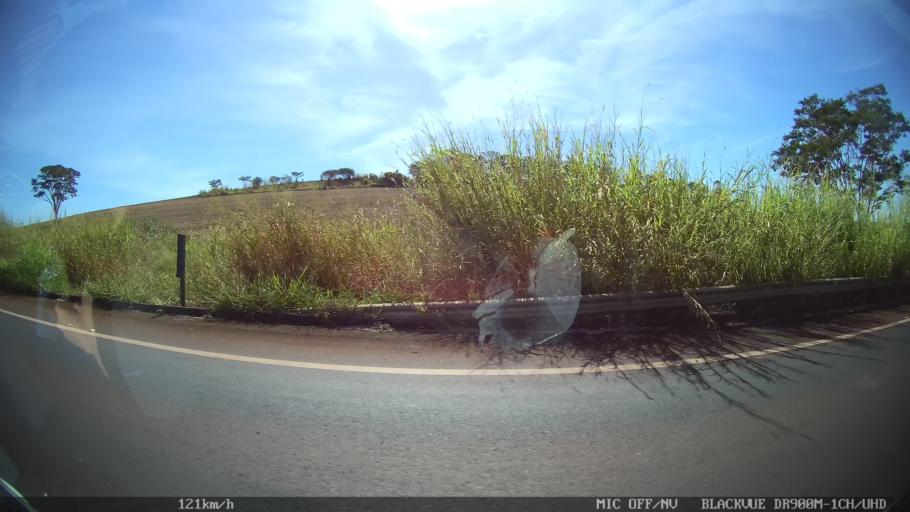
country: BR
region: Sao Paulo
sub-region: Sao Joaquim Da Barra
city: Sao Joaquim da Barra
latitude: -20.5612
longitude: -47.6863
